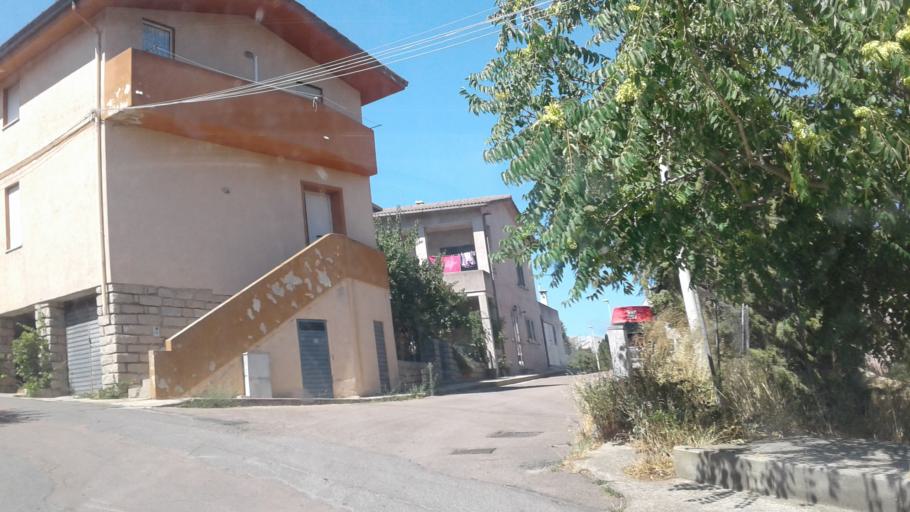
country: IT
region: Sardinia
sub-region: Provincia di Olbia-Tempio
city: Aggius
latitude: 40.9292
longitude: 9.0688
